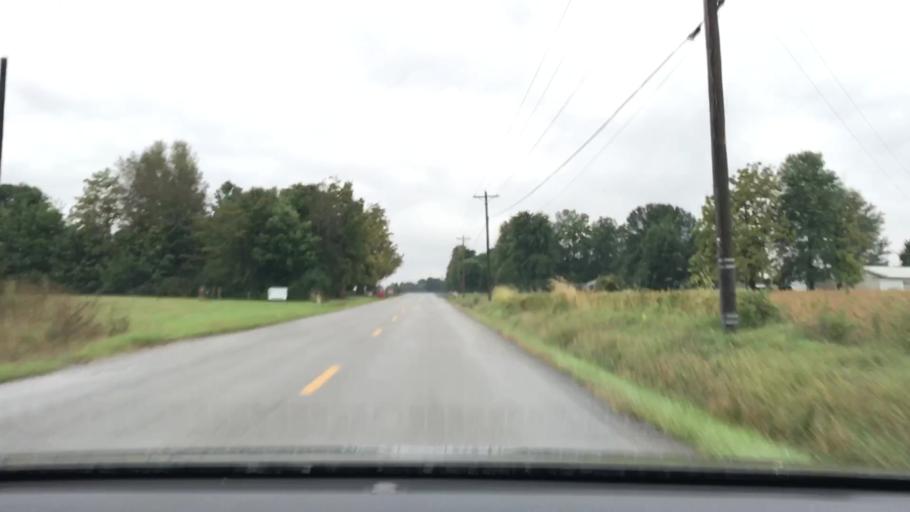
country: US
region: Kentucky
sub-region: McLean County
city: Calhoun
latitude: 37.4399
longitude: -87.2465
